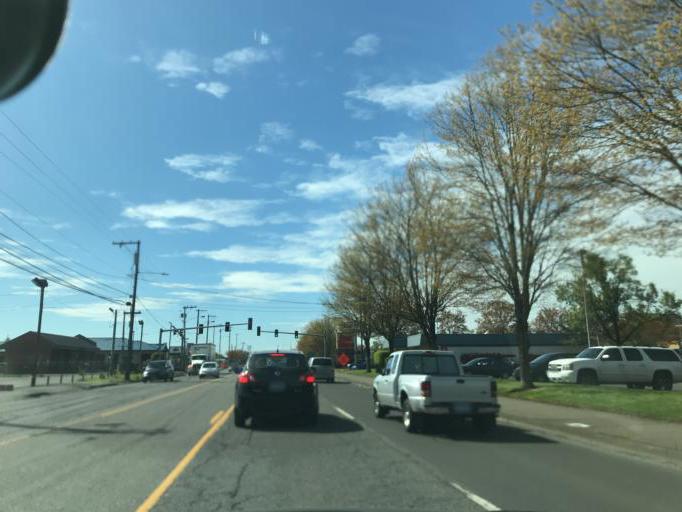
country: US
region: Oregon
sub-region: Multnomah County
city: Lents
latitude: 45.4598
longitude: -122.5791
